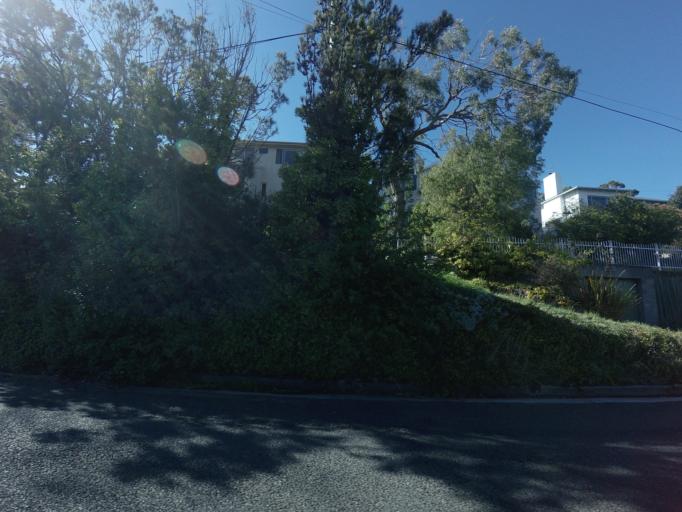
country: AU
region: Tasmania
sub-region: Clarence
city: Lindisfarne
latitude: -42.8453
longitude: 147.3396
